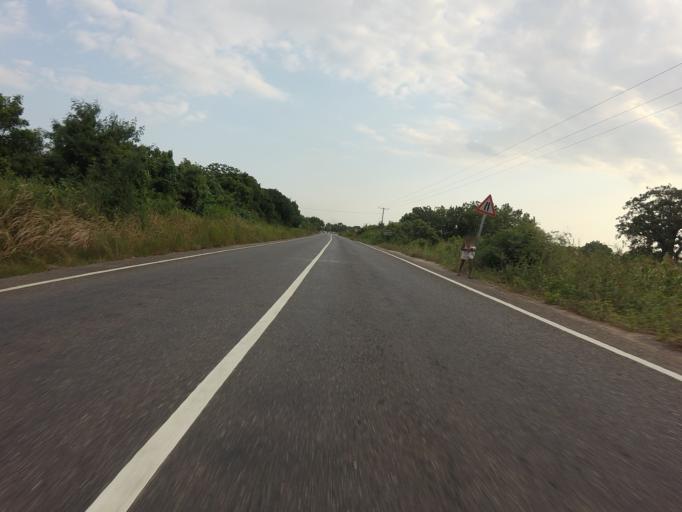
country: GH
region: Volta
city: Anloga
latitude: 6.1074
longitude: 0.5152
